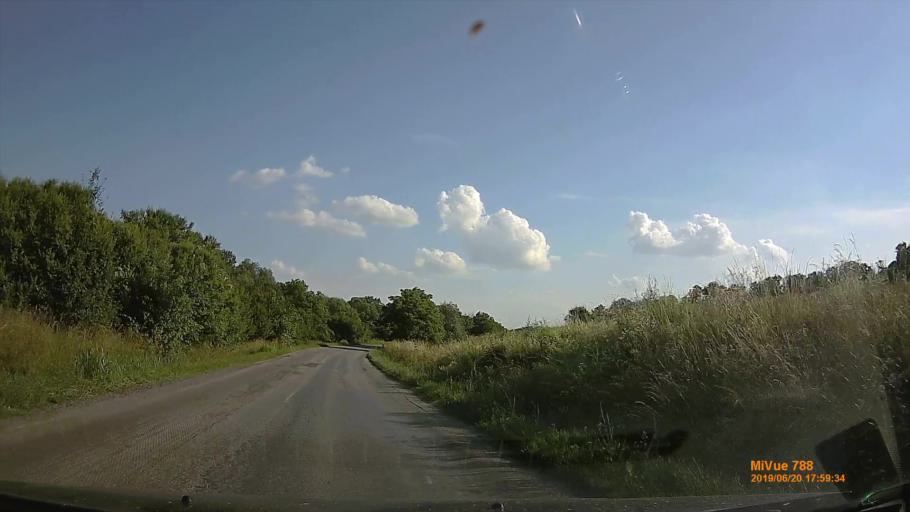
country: HU
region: Baranya
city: Buekkoesd
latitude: 46.0960
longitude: 17.9857
